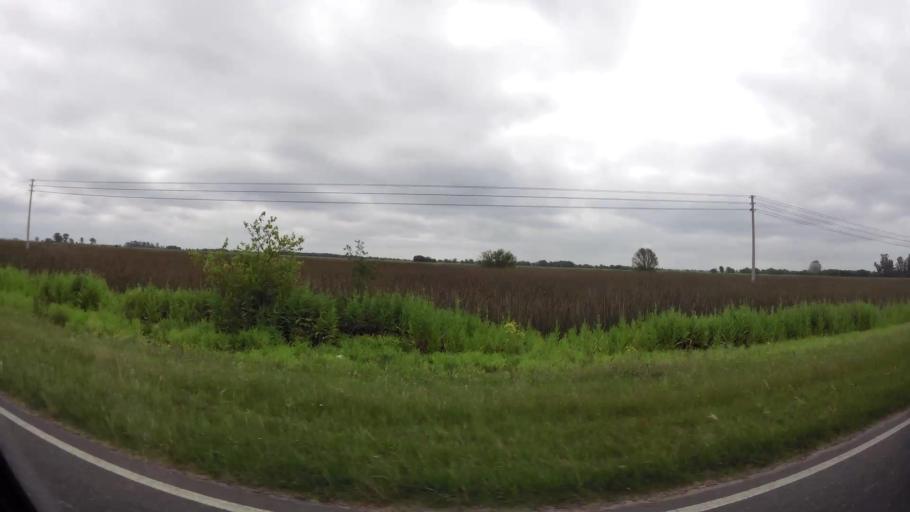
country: AR
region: Buenos Aires
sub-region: Partido de San Vicente
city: San Vicente
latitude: -34.9906
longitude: -58.4688
